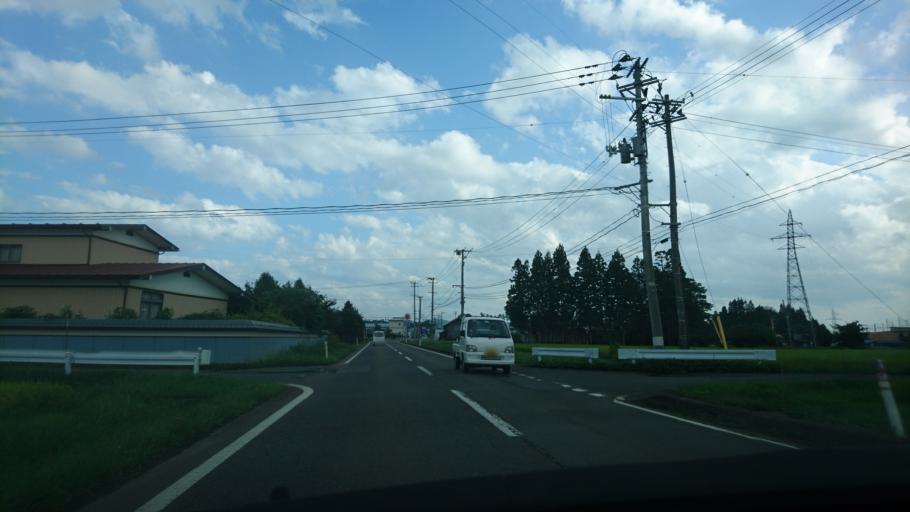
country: JP
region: Iwate
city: Hanamaki
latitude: 39.3405
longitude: 141.1522
